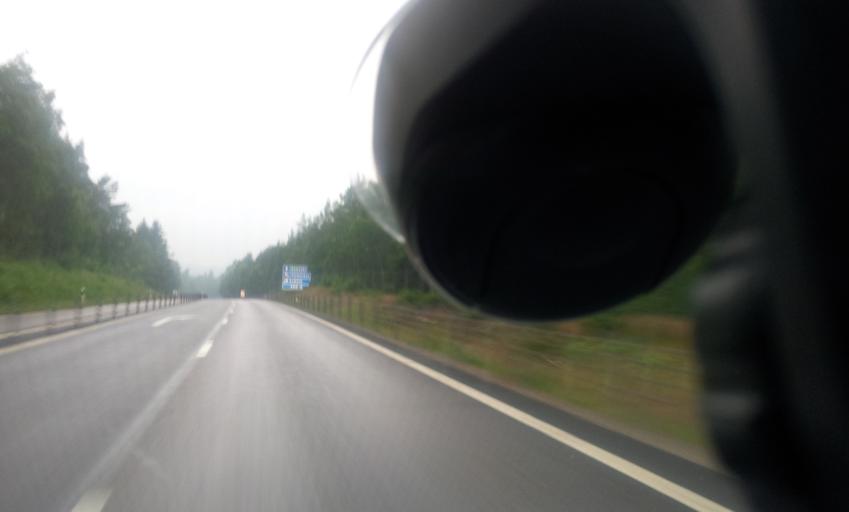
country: SE
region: Kalmar
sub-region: Vasterviks Kommun
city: Gamleby
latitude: 57.8246
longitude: 16.4580
